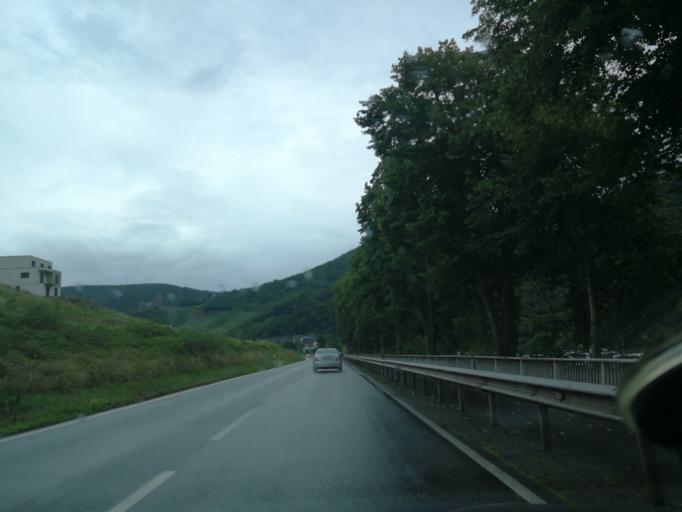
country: DE
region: Rheinland-Pfalz
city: Monzelfeld
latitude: 49.9101
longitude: 7.0545
